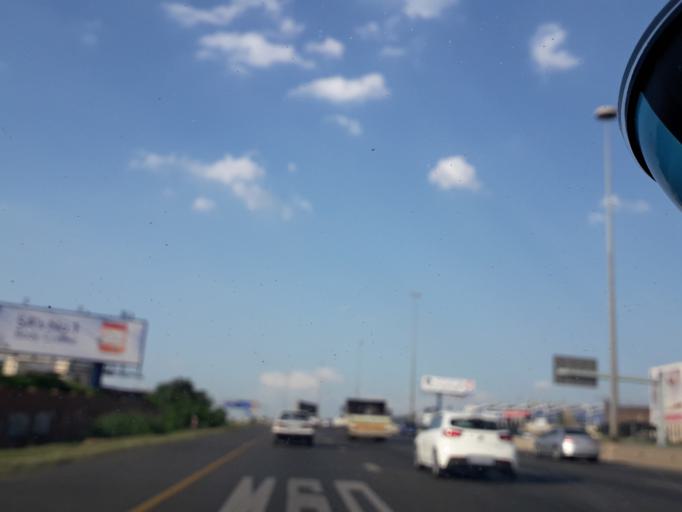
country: ZA
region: Gauteng
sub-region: City of Johannesburg Metropolitan Municipality
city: Modderfontein
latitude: -26.0969
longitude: 28.0828
